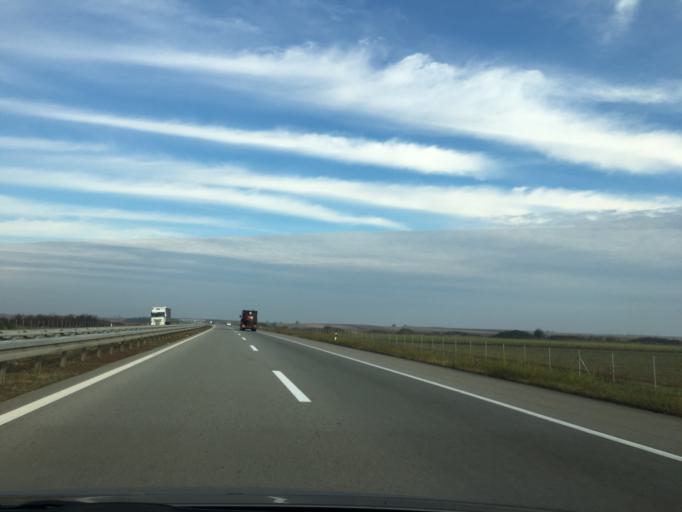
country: RS
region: Autonomna Pokrajina Vojvodina
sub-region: Juznobacki Okrug
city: Kovilj
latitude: 45.2204
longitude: 20.0607
